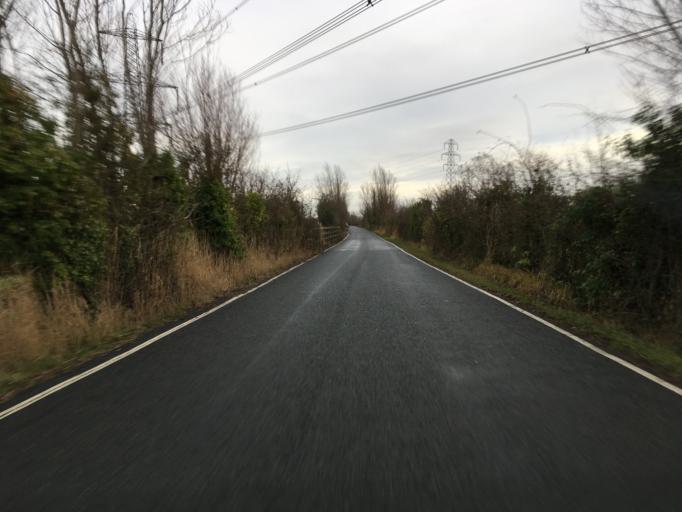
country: GB
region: Wales
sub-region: Newport
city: Bishton
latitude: 51.5639
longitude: -2.8987
